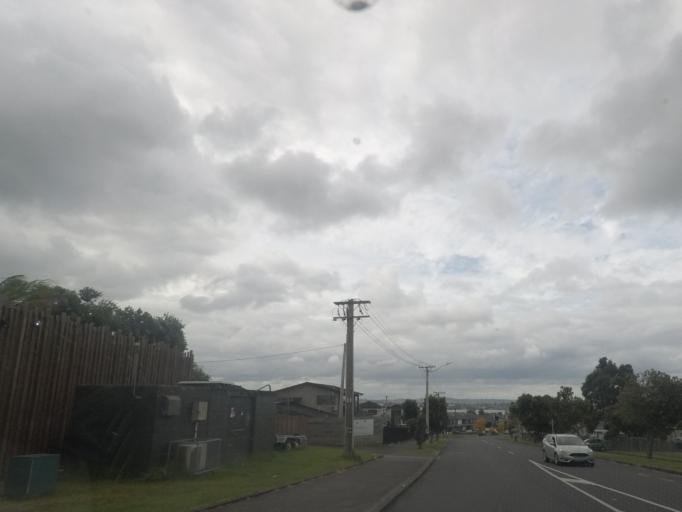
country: NZ
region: Auckland
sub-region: Auckland
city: Tamaki
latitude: -36.8696
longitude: 174.8744
